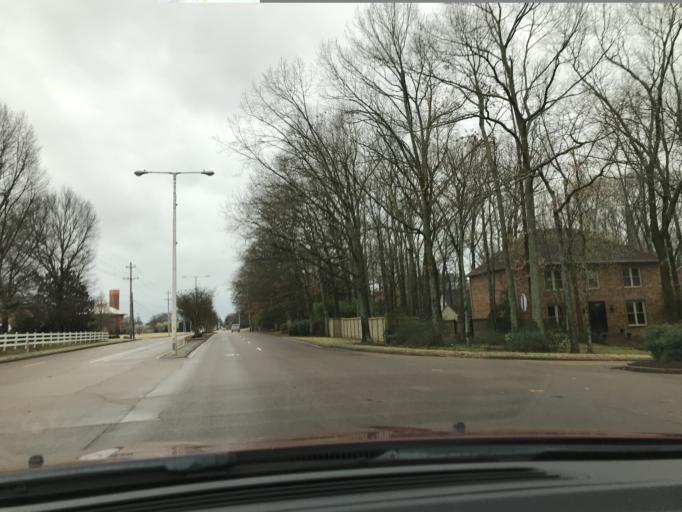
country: US
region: Tennessee
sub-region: Shelby County
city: Collierville
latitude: 35.0653
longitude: -89.6859
